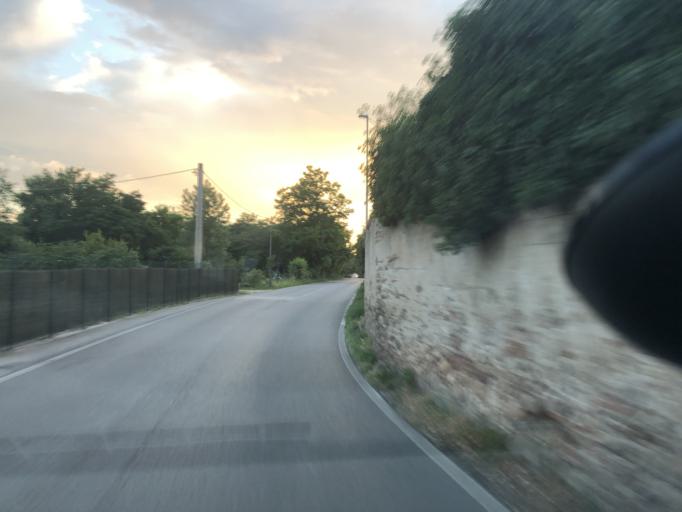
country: IT
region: Veneto
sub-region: Provincia di Verona
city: San Vito al Mantico
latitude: 45.4721
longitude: 10.8819
